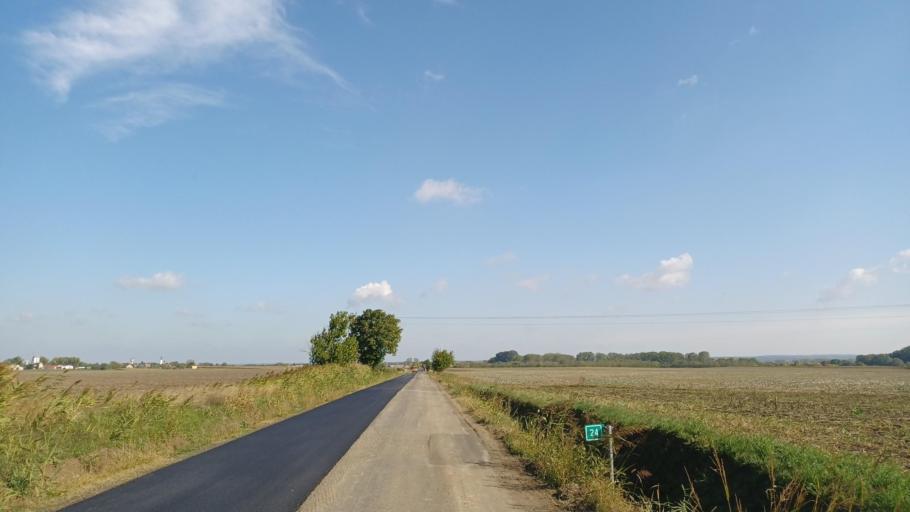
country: HU
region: Tolna
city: Nagydorog
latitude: 46.6083
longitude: 18.5959
